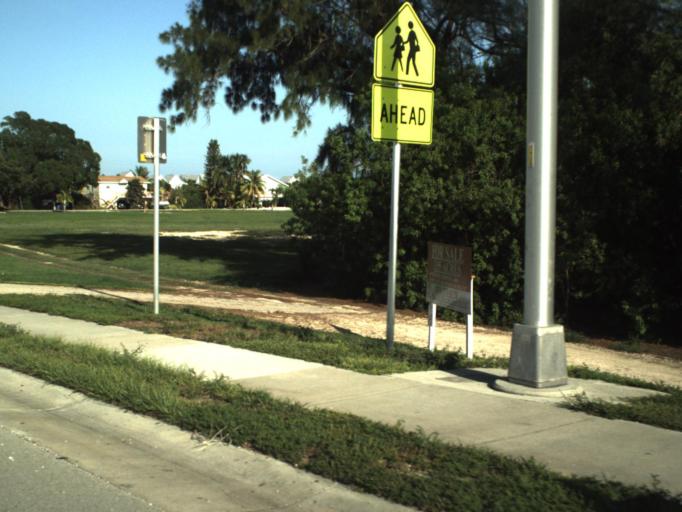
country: US
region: Florida
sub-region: Monroe County
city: Marathon
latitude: 24.7306
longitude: -81.0283
